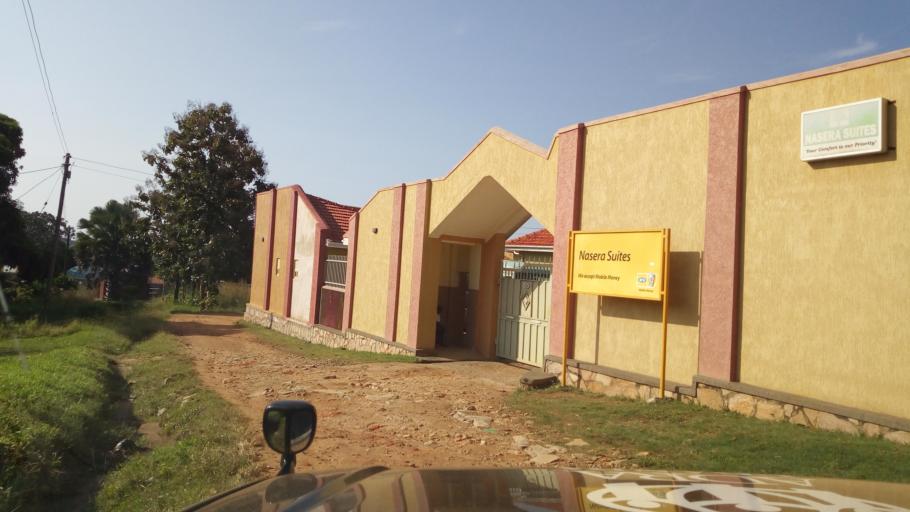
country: UG
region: Northern Region
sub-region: Moyo District
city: Moyo
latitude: 3.6475
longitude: 31.7269
